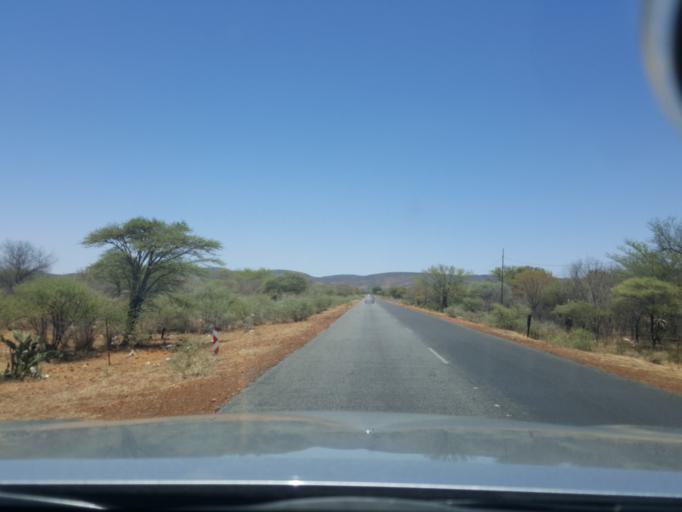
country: BW
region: South East
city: Lobatse
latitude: -25.2587
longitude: 25.9280
